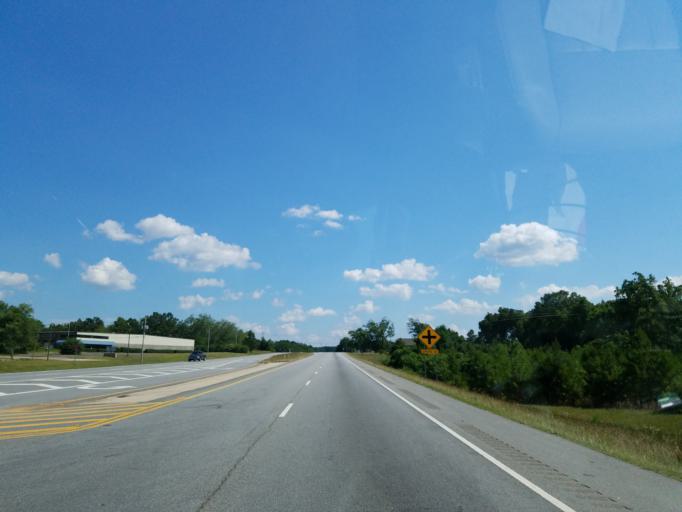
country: US
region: Georgia
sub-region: Lamar County
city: Barnesville
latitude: 33.0672
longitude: -84.1695
